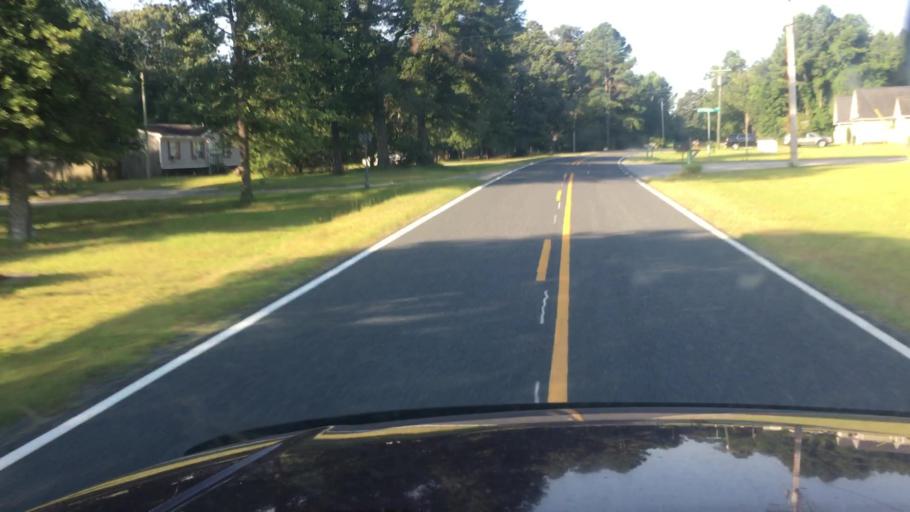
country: US
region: North Carolina
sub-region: Robeson County
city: Saint Pauls
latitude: 34.8423
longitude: -78.8889
